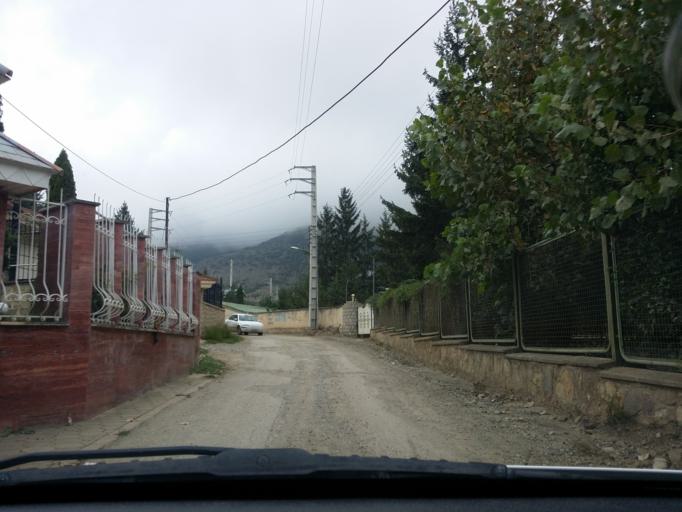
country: IR
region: Mazandaran
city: `Abbasabad
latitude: 36.4903
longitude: 51.1406
